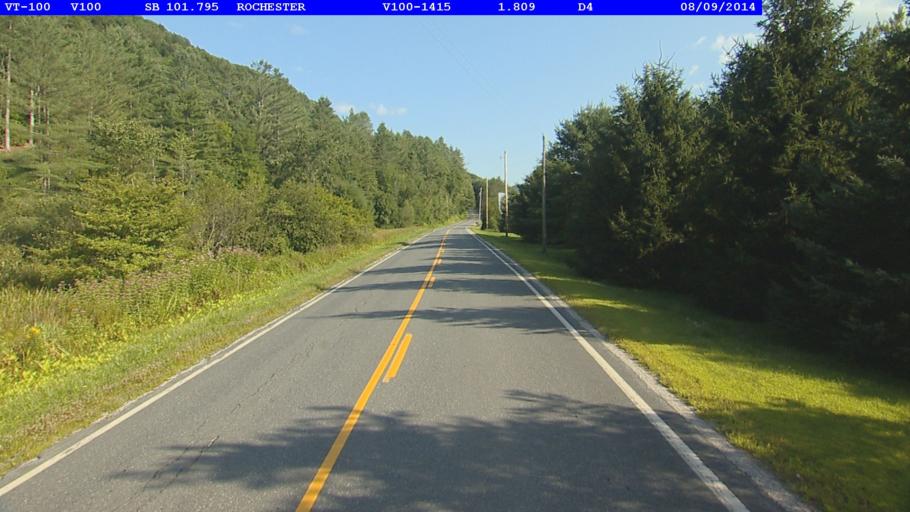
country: US
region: Vermont
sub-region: Orange County
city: Randolph
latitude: 43.8286
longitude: -72.7928
